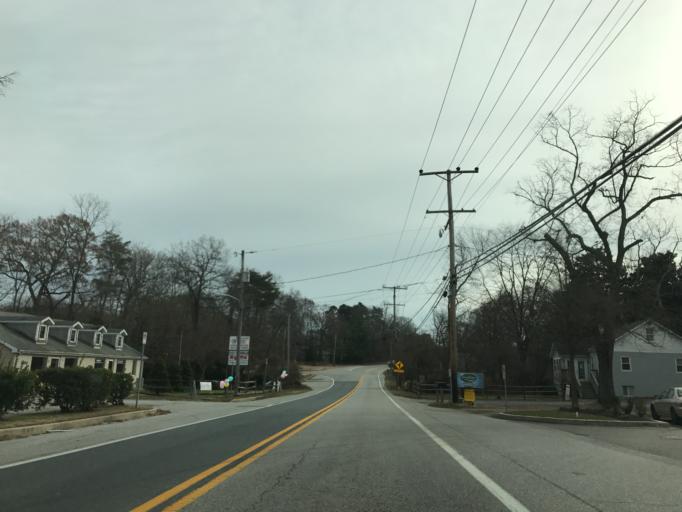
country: US
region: Maryland
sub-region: Anne Arundel County
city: Pasadena
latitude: 39.1087
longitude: -76.5546
